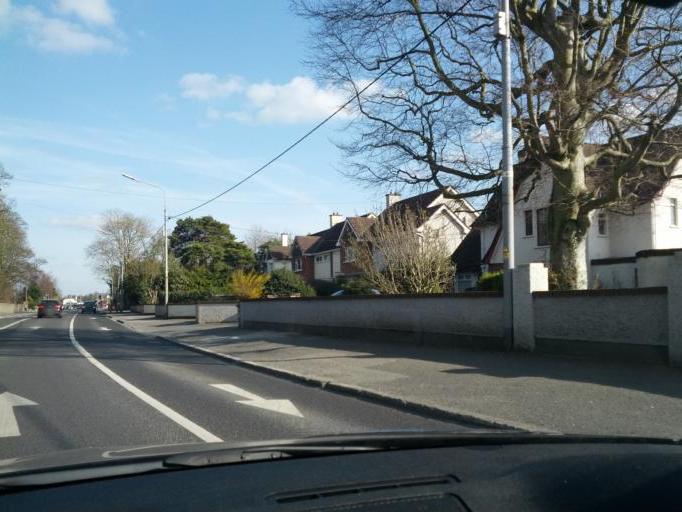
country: IE
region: Leinster
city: Lucan
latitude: 53.3601
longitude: -6.4364
